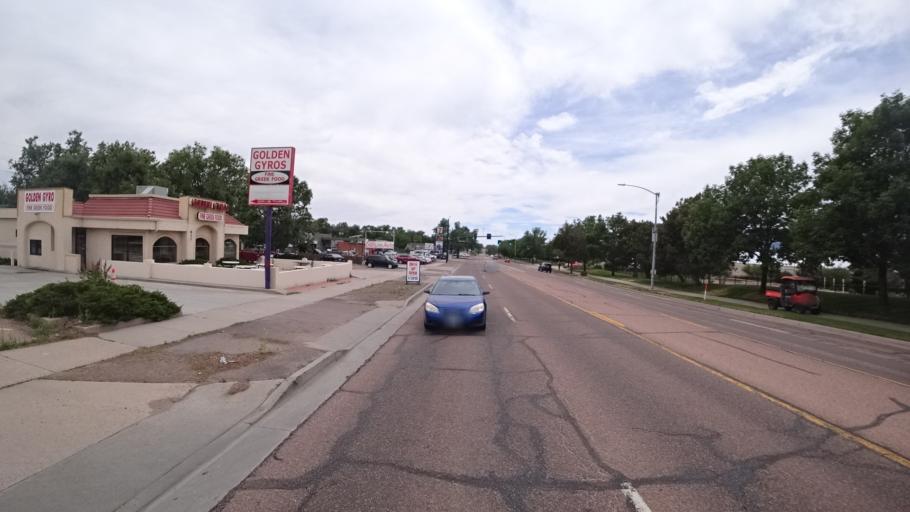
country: US
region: Colorado
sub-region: El Paso County
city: Colorado Springs
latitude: 38.8417
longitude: -104.7942
